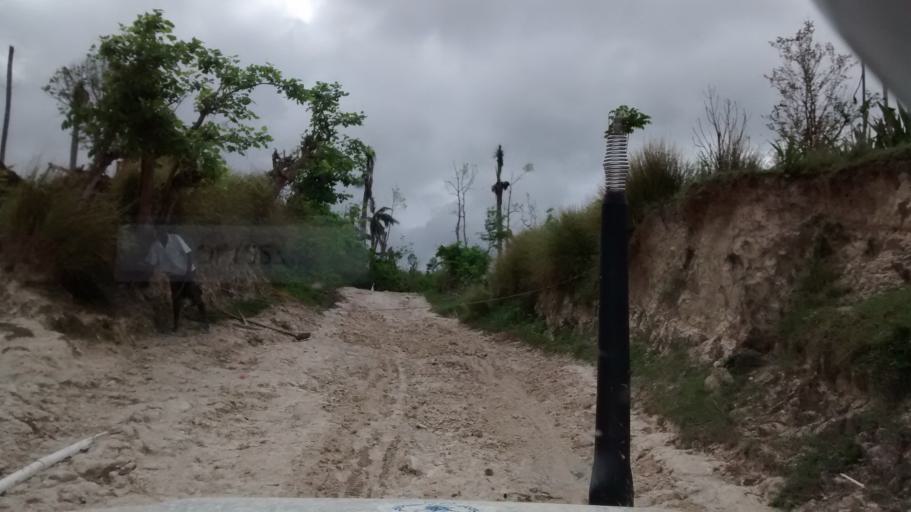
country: HT
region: Grandans
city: Jeremie
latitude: 18.5837
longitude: -74.1481
